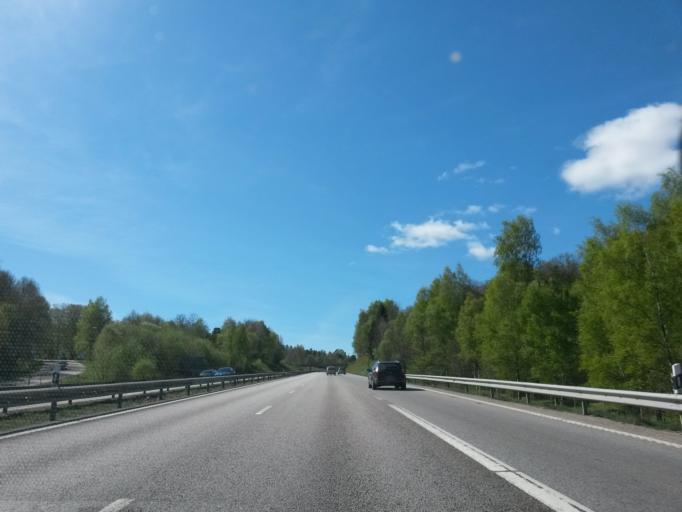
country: SE
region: Vaestra Goetaland
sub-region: Lerums Kommun
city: Lerum
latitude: 57.7507
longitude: 12.2413
